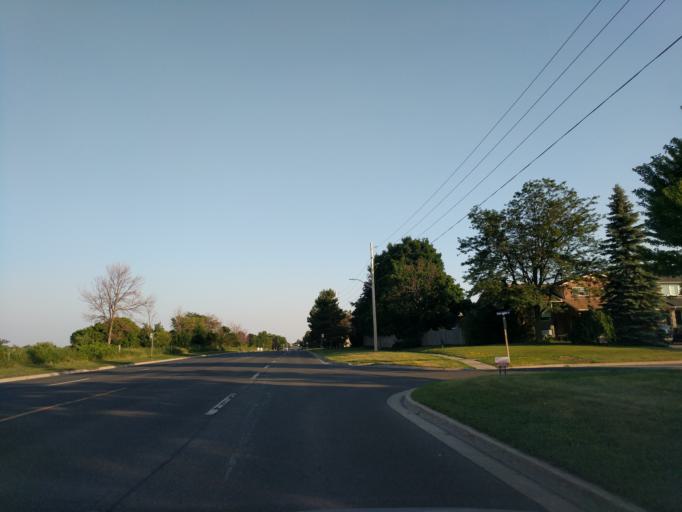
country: CA
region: Ontario
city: Oshawa
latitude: 43.9153
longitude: -78.9035
